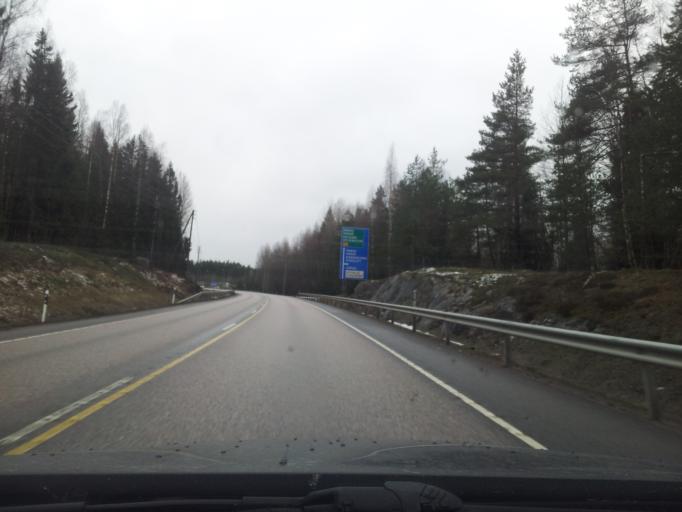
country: FI
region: Uusimaa
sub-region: Helsinki
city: Kirkkonummi
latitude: 60.1450
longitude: 24.5379
